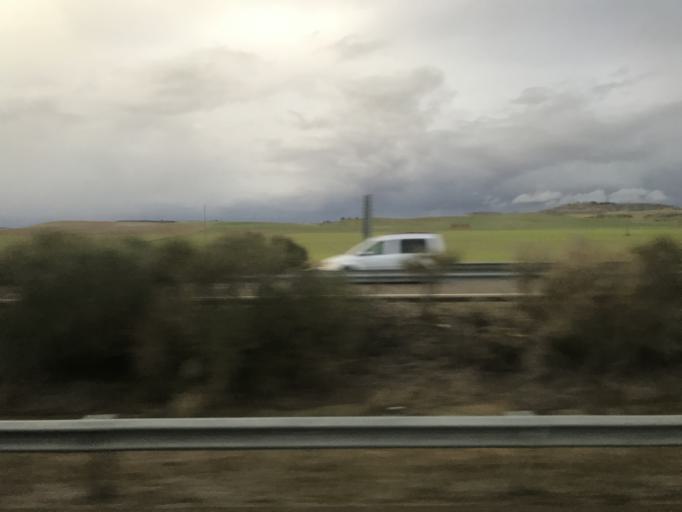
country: ES
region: Castille and Leon
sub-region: Provincia de Palencia
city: Torquemada
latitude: 42.0183
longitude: -4.3404
